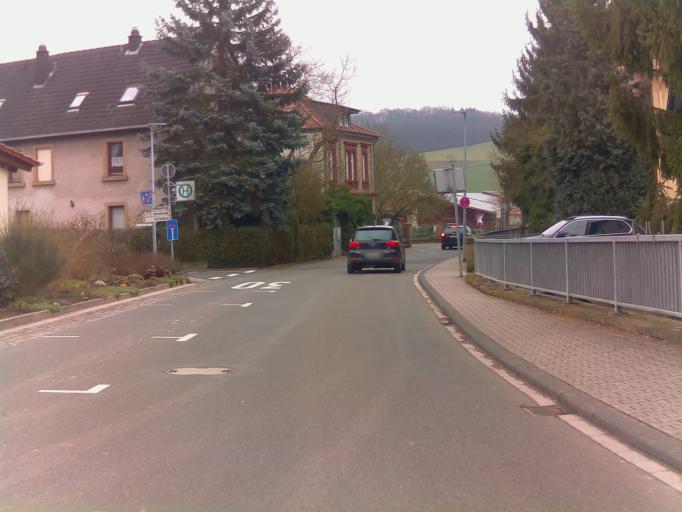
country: DE
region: Rheinland-Pfalz
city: Raumbach
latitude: 49.7242
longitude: 7.6623
